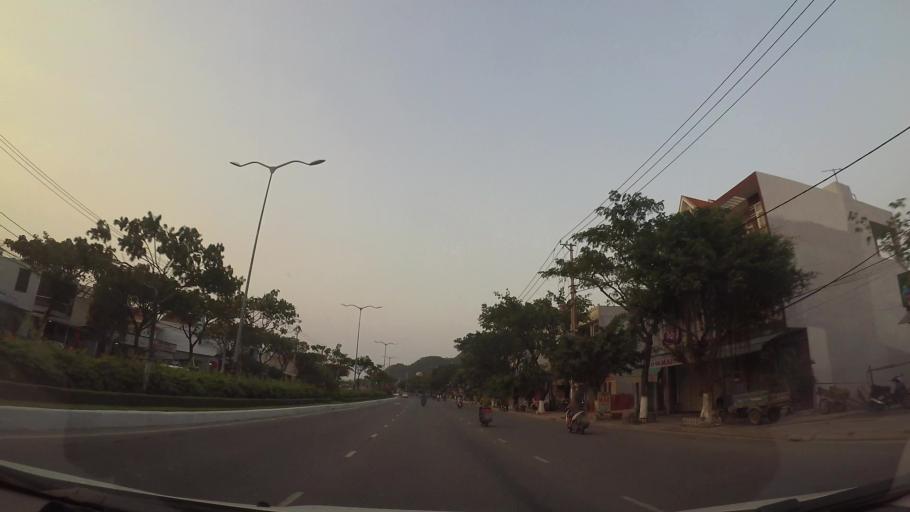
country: VN
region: Da Nang
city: Ngu Hanh Son
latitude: 15.9982
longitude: 108.2595
